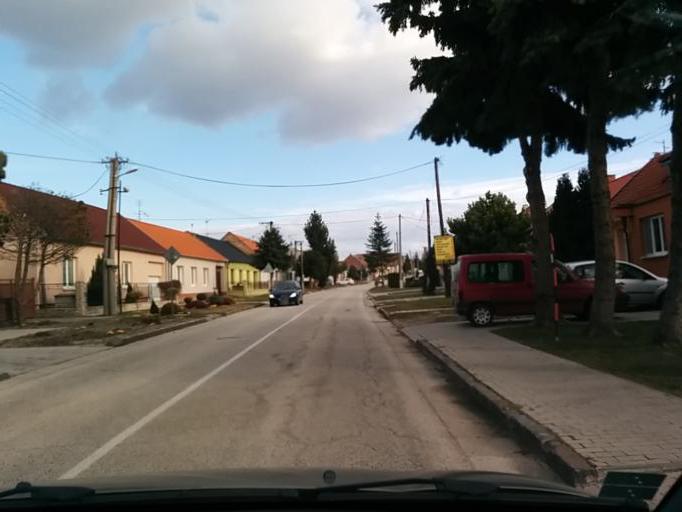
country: SK
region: Trnavsky
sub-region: Okres Trnava
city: Trnava
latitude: 48.3331
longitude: 17.5939
